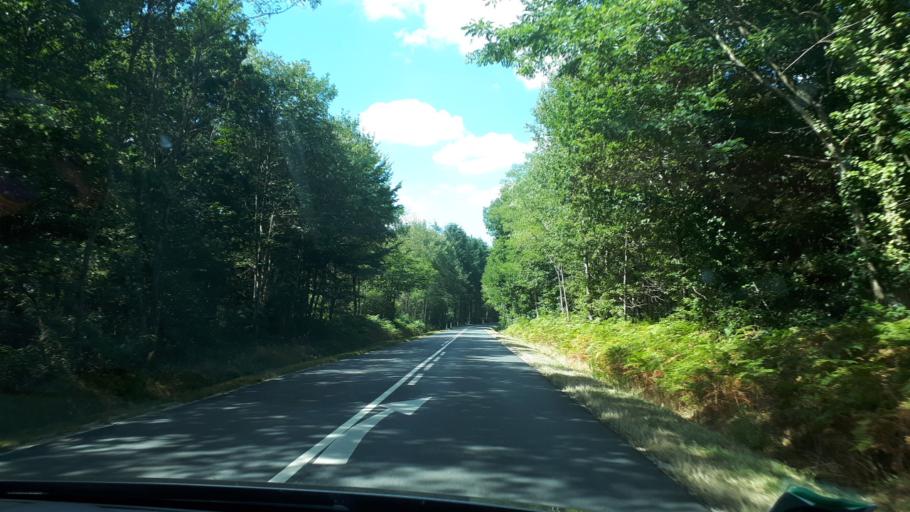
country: FR
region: Centre
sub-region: Departement du Loir-et-Cher
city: Saint-Viatre
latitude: 47.5614
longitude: 1.9032
